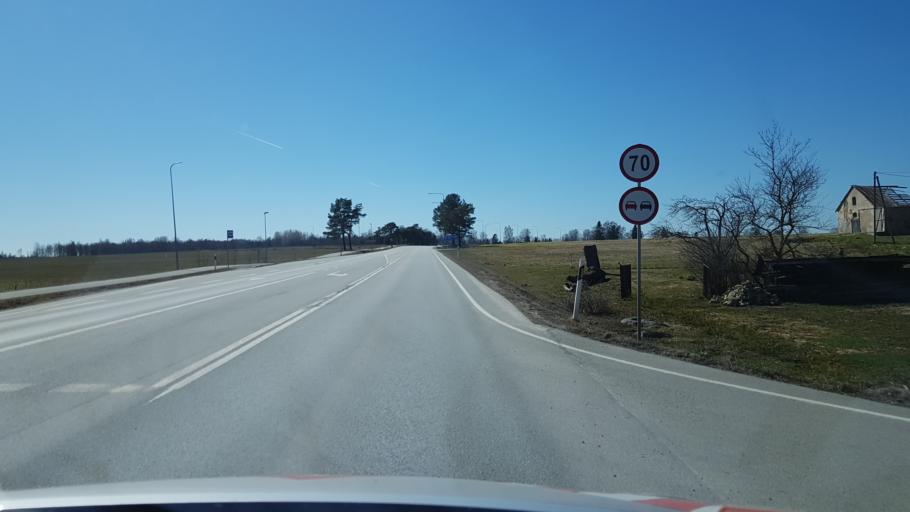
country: EE
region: Laeaene-Virumaa
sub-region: Rakvere linn
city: Rakvere
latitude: 59.4183
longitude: 26.3461
